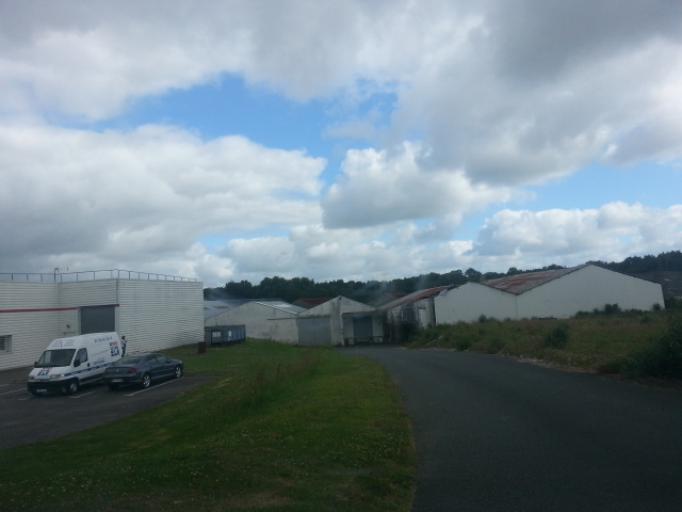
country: FR
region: Brittany
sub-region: Departement du Finistere
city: Rosporden
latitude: 47.9641
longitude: -3.8484
